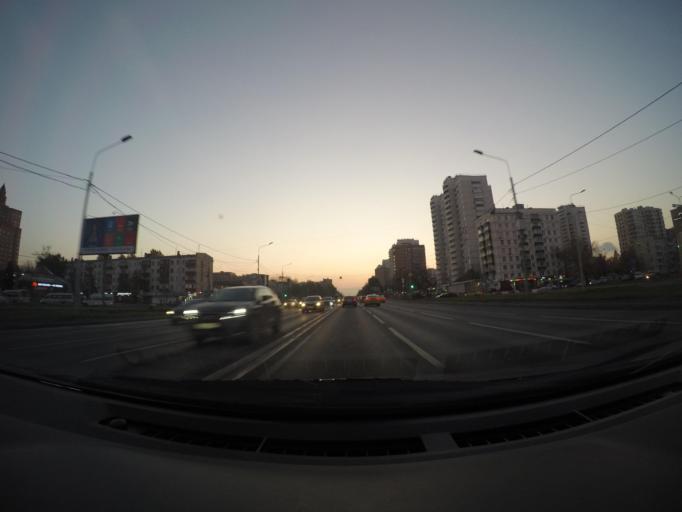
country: RU
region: Moscow
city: Novyye Kuz'minki
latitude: 55.7055
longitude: 37.7654
